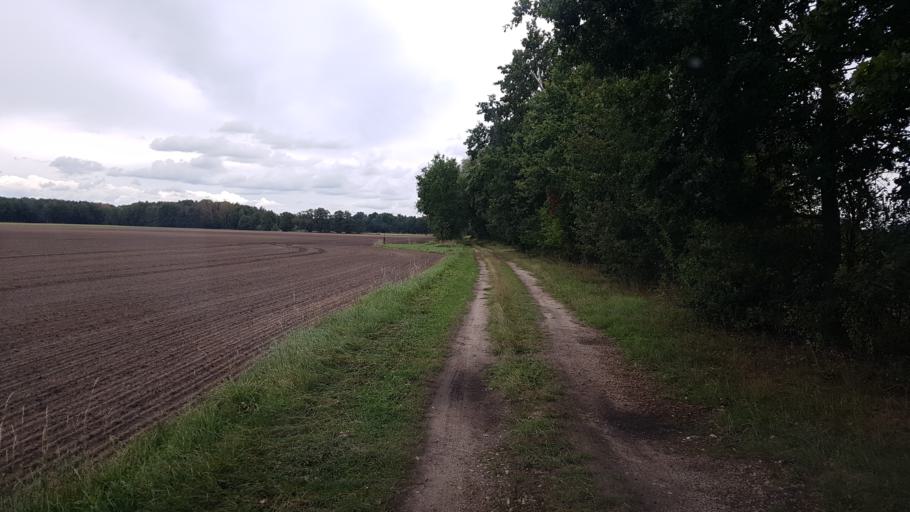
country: DE
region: Brandenburg
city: Doberlug-Kirchhain
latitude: 51.6491
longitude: 13.5852
